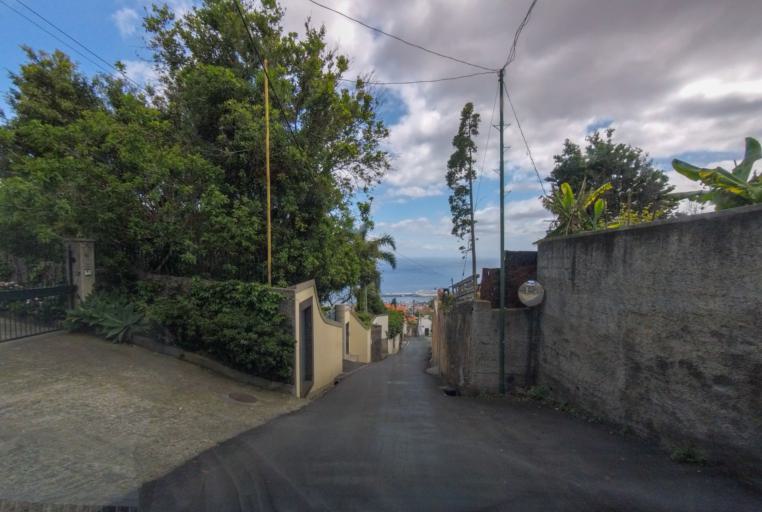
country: PT
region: Madeira
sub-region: Funchal
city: Nossa Senhora do Monte
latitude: 32.6650
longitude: -16.9045
